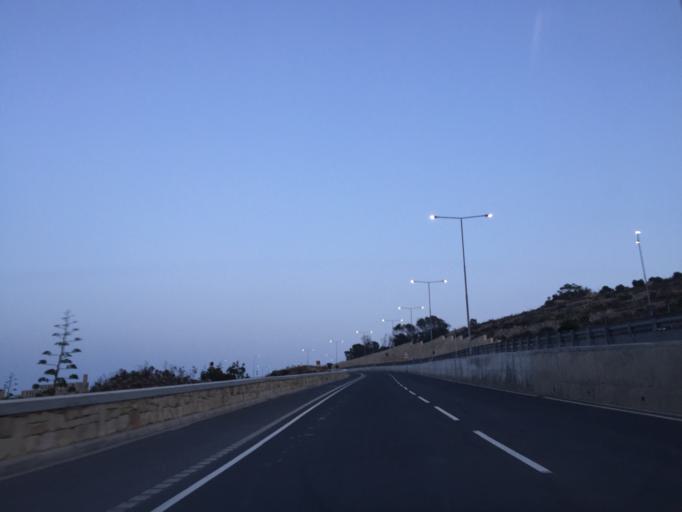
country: MT
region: Pembroke
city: Pembroke
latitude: 35.9342
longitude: 14.4626
